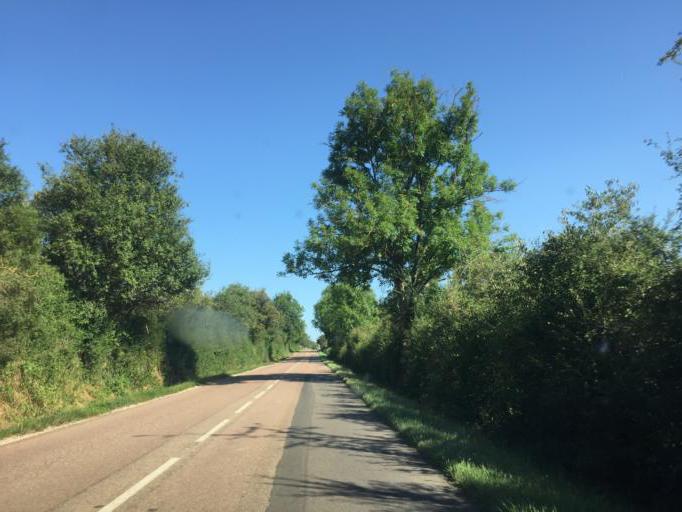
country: FR
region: Bourgogne
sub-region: Departement de l'Yonne
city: Fontenailles
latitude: 47.4735
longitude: 3.4403
